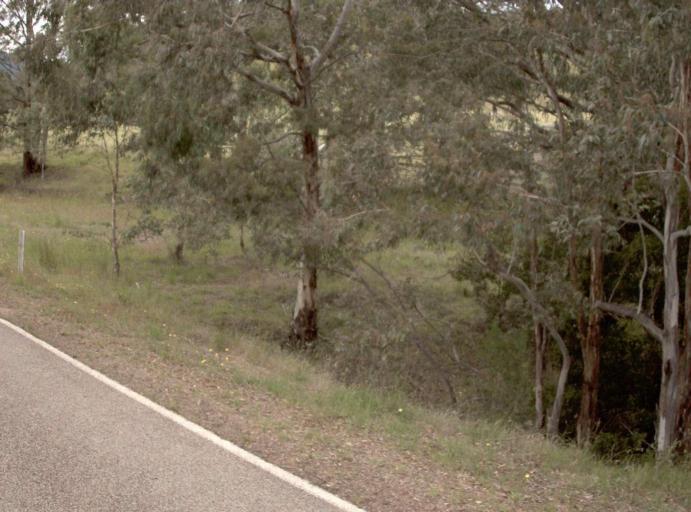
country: AU
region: Victoria
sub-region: East Gippsland
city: Bairnsdale
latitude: -37.5464
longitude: 147.2017
